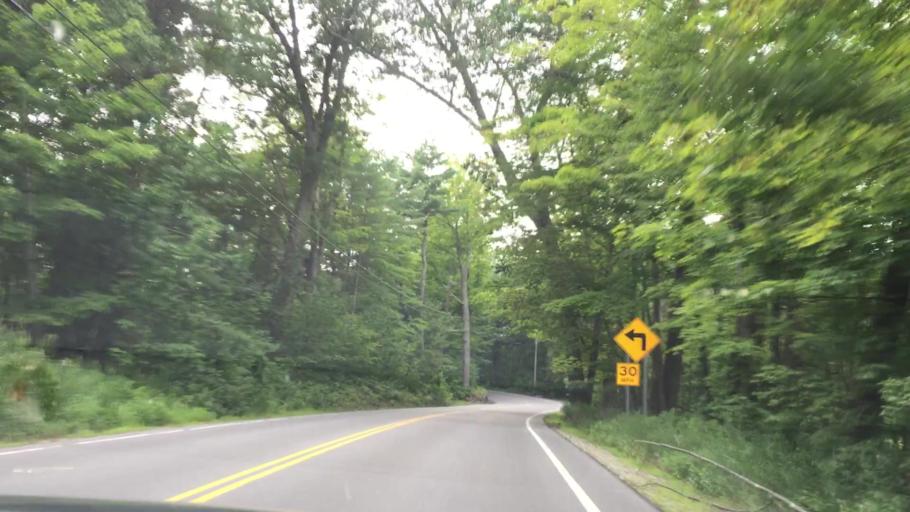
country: US
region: New Hampshire
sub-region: Belknap County
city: Meredith
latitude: 43.7036
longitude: -71.5086
